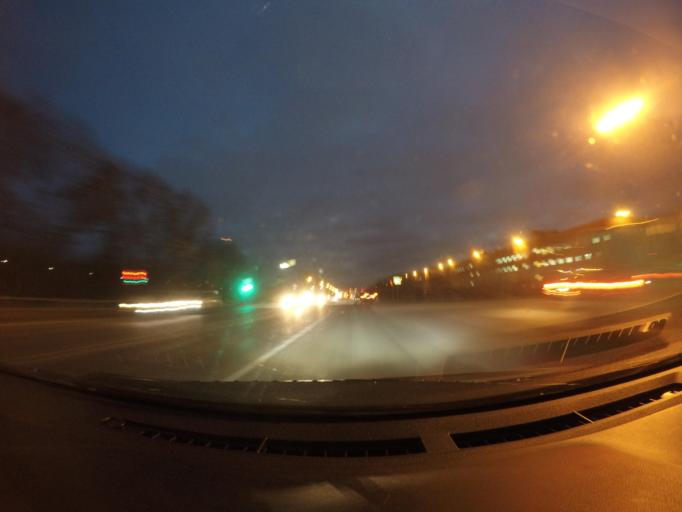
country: RU
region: Moskovskaya
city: Petrovskaya
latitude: 55.5686
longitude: 37.7636
